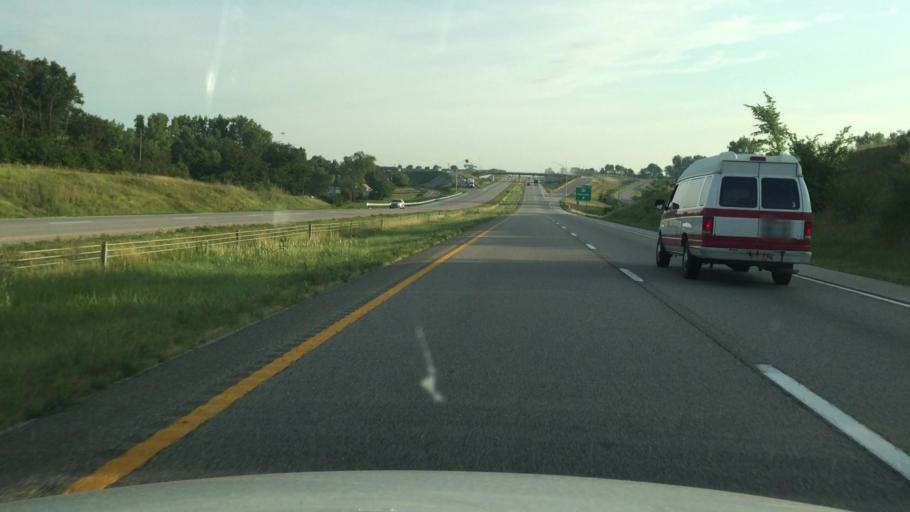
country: US
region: Kansas
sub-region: Doniphan County
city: Elwood
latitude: 39.5936
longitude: -94.7887
